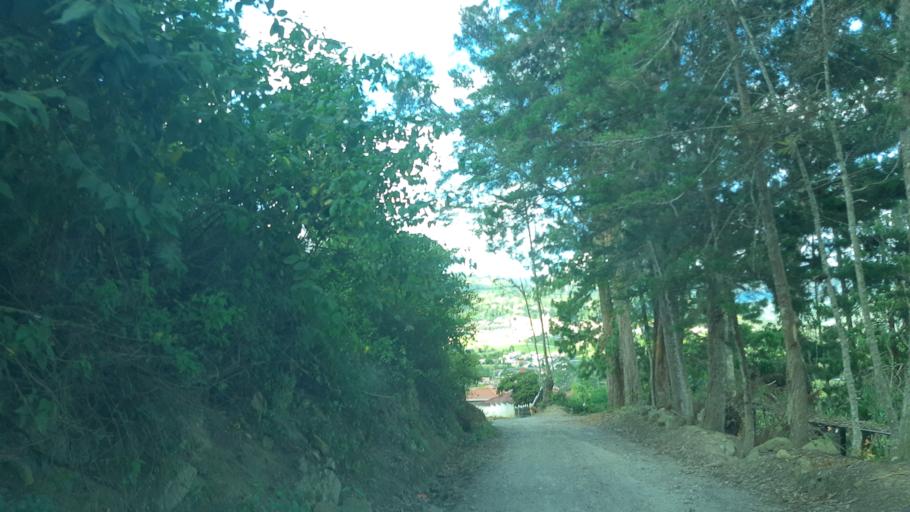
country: CO
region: Cundinamarca
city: Macheta
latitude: 5.0731
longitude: -73.6195
